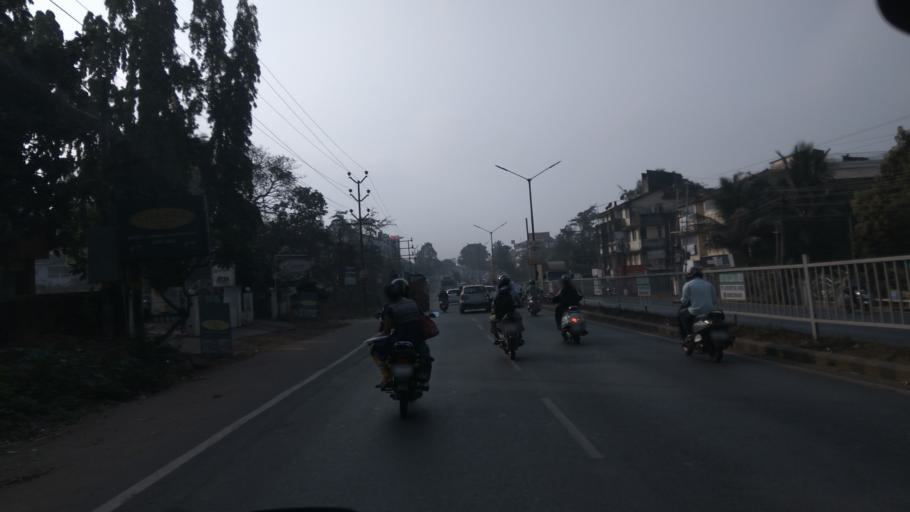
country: IN
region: Goa
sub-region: North Goa
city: Serula
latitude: 15.5294
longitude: 73.8255
